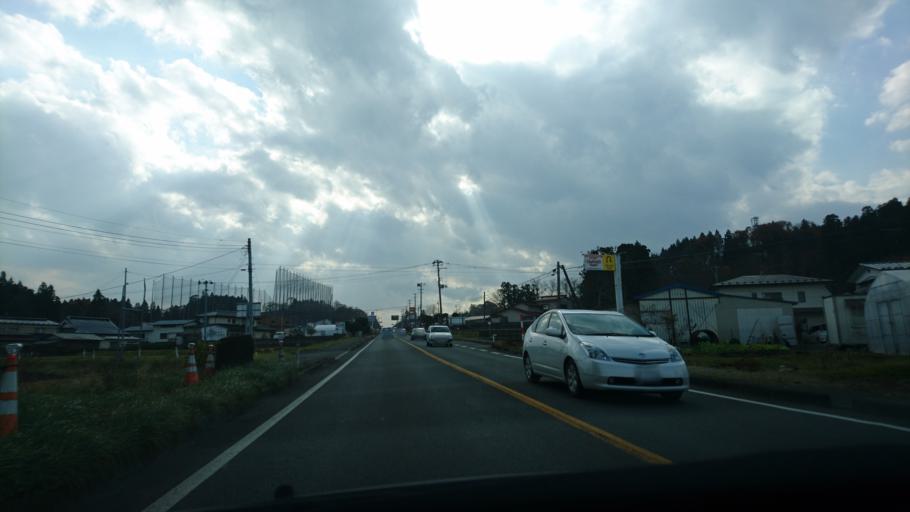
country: JP
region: Iwate
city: Mizusawa
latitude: 39.0354
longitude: 141.1183
